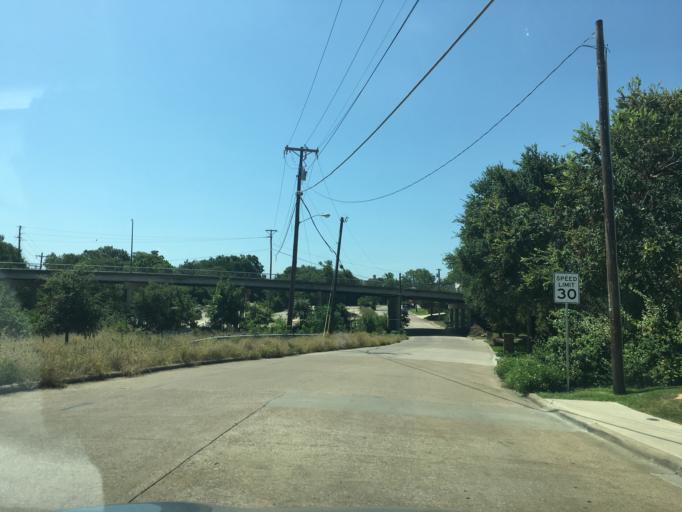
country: US
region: Texas
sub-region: Dallas County
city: Highland Park
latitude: 32.8449
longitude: -96.7400
